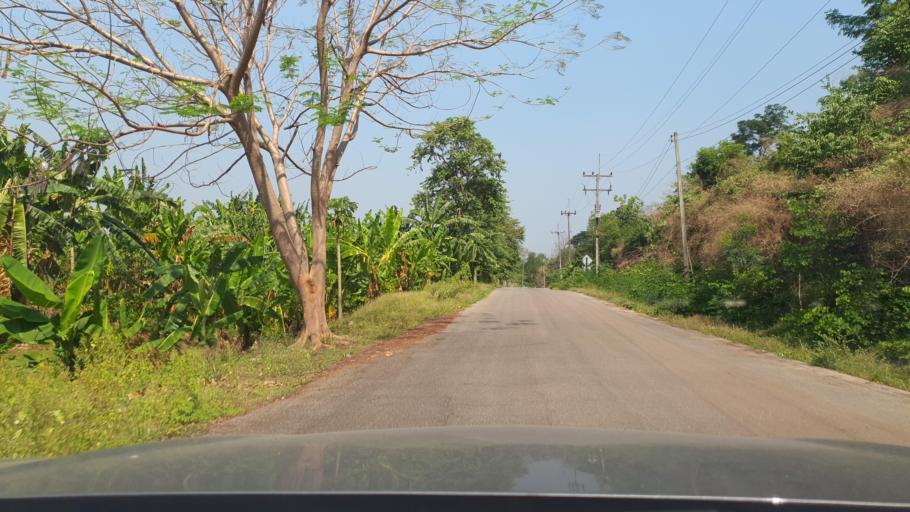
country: TH
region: Kanchanaburi
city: Sai Yok
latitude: 14.0973
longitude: 99.1737
